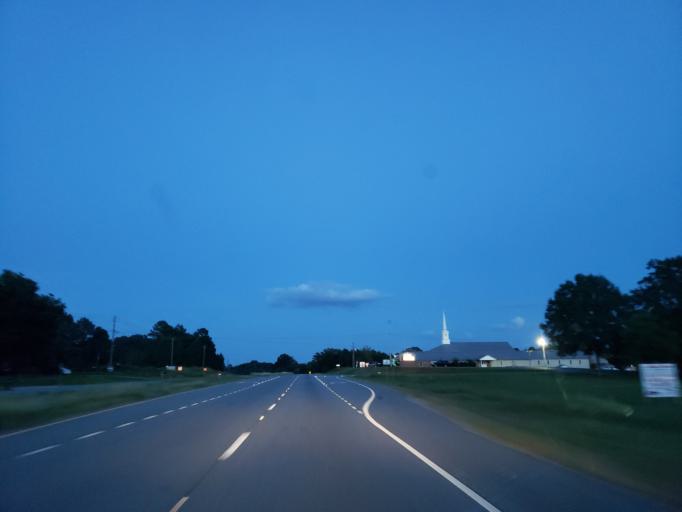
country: US
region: Georgia
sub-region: Polk County
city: Aragon
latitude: 34.0038
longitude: -85.1557
